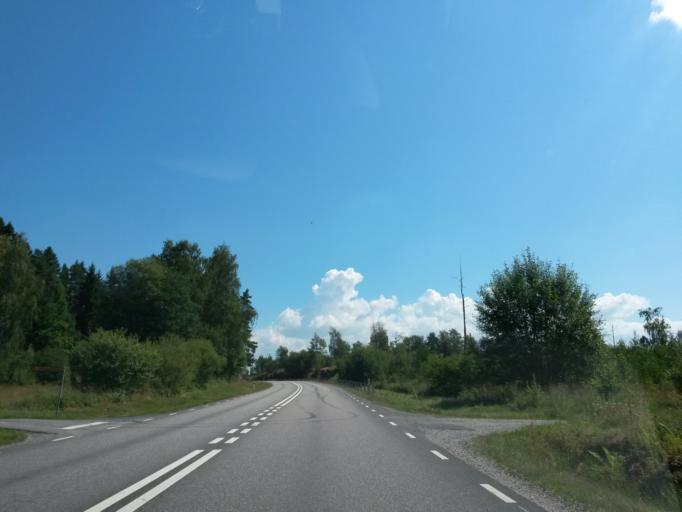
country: SE
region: Vaestra Goetaland
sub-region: Grastorps Kommun
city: Graestorp
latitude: 58.3233
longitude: 12.7461
